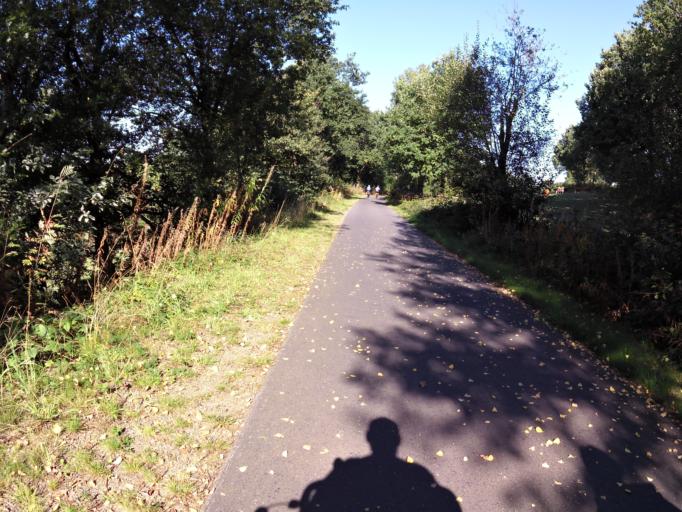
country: BE
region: Wallonia
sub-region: Province de Liege
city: Waimes
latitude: 50.3931
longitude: 6.1226
